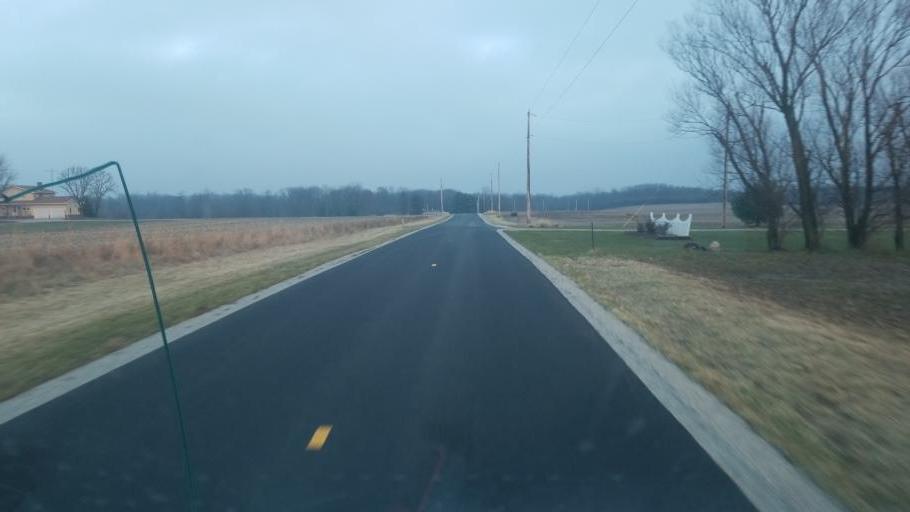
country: US
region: Ohio
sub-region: Seneca County
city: Tiffin
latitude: 41.0073
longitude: -83.2526
